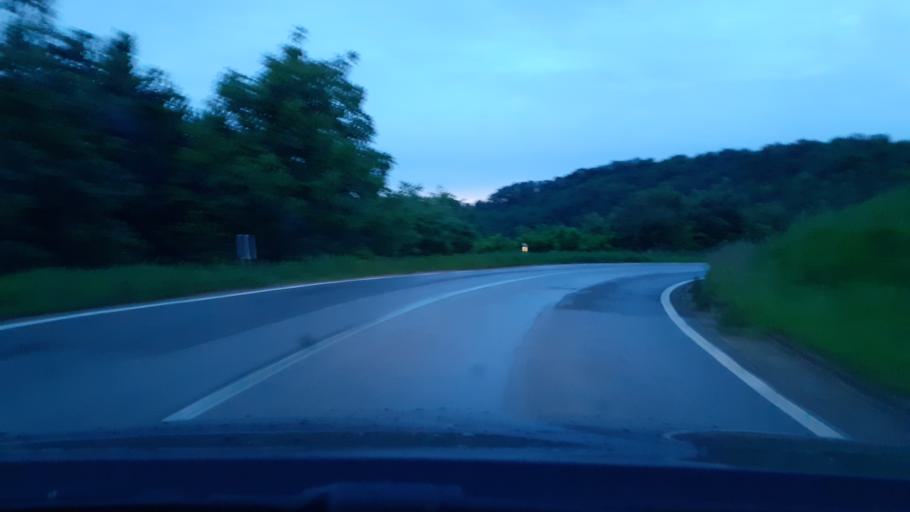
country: HR
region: Pozesko-Slavonska
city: Bilice
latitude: 45.2250
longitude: 17.8490
